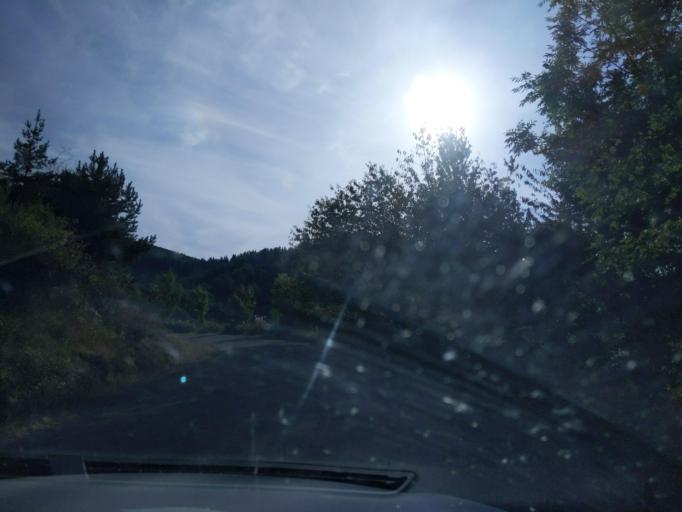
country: ES
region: La Rioja
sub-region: Provincia de La Rioja
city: Ezcaray
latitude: 42.3209
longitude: -3.0243
